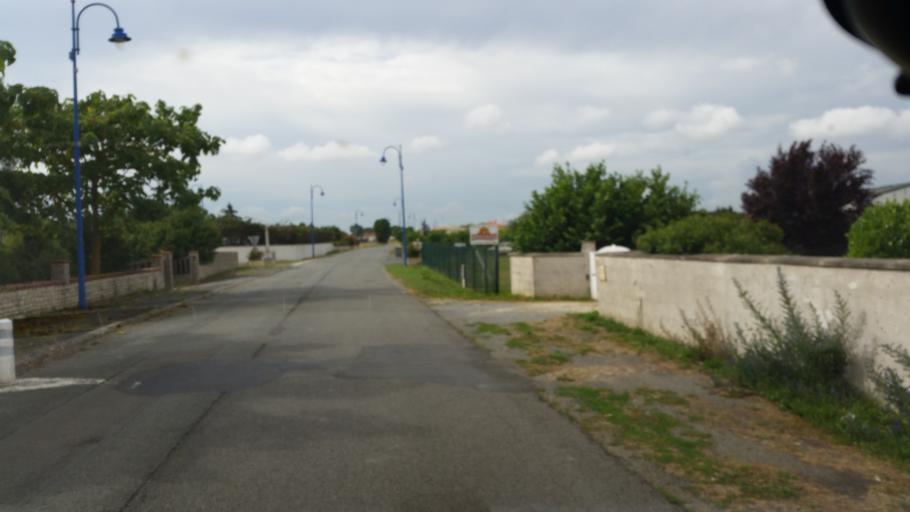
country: FR
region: Poitou-Charentes
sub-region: Departement de la Charente-Maritime
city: Courcon
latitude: 46.1915
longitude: -0.8655
